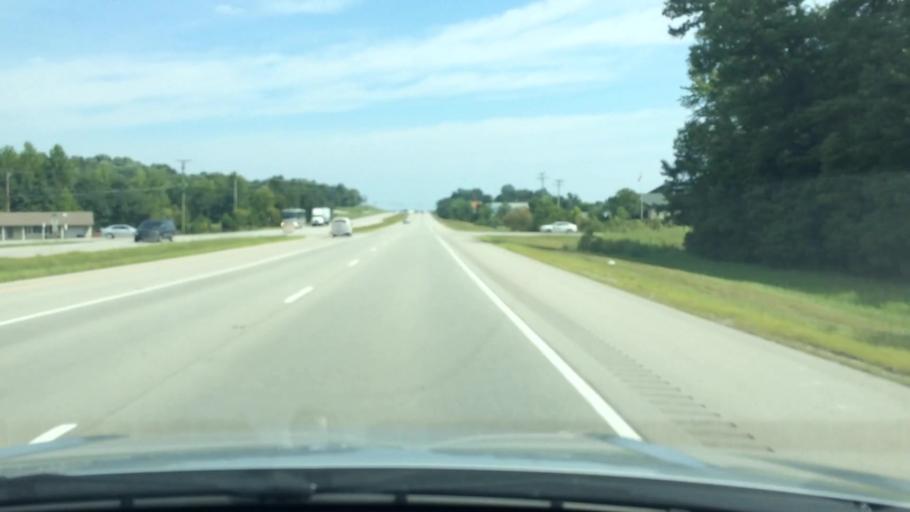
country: US
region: Kentucky
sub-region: Franklin County
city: Frankfort
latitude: 38.1429
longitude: -84.9010
